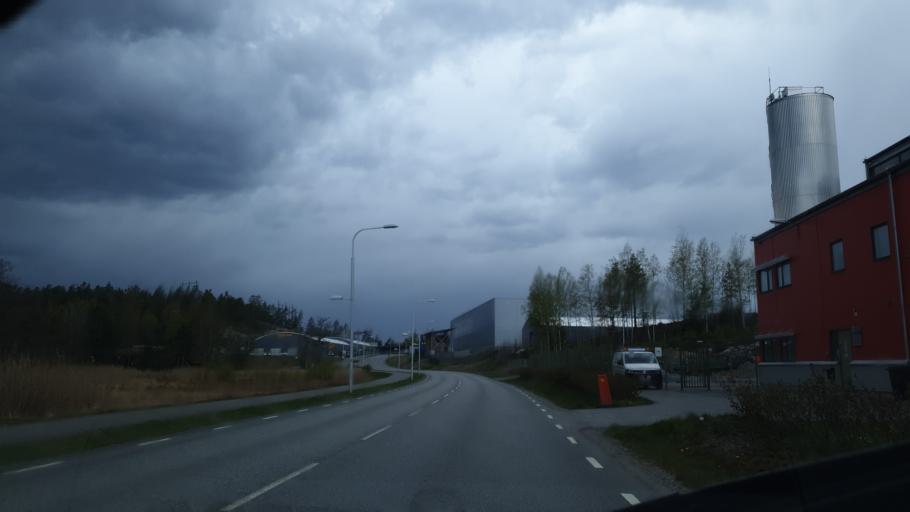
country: SE
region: Stockholm
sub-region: Varmdo Kommun
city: Gustavsberg
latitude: 59.3127
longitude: 18.3780
